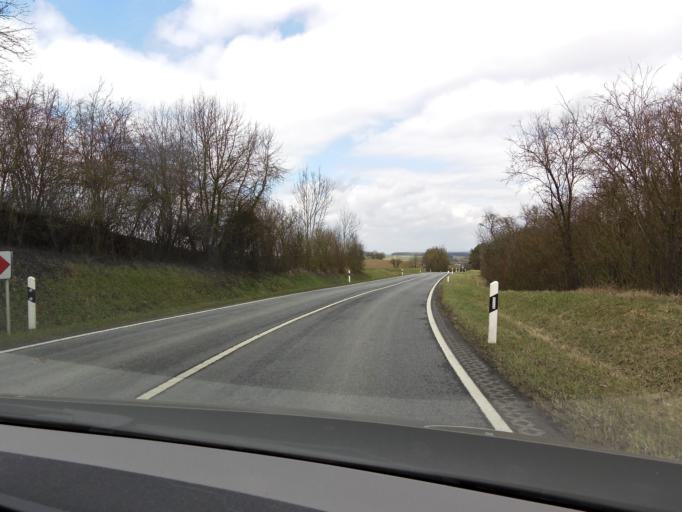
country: DE
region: Bavaria
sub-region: Regierungsbezirk Unterfranken
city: Arnstein
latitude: 49.9638
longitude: 9.9780
